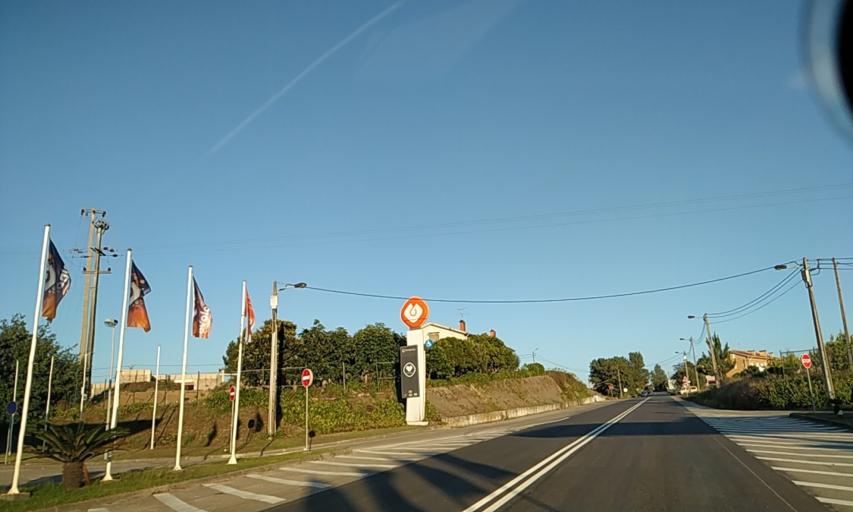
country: PT
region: Aveiro
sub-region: Oliveira do Bairro
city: Oia
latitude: 40.5510
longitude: -8.5445
